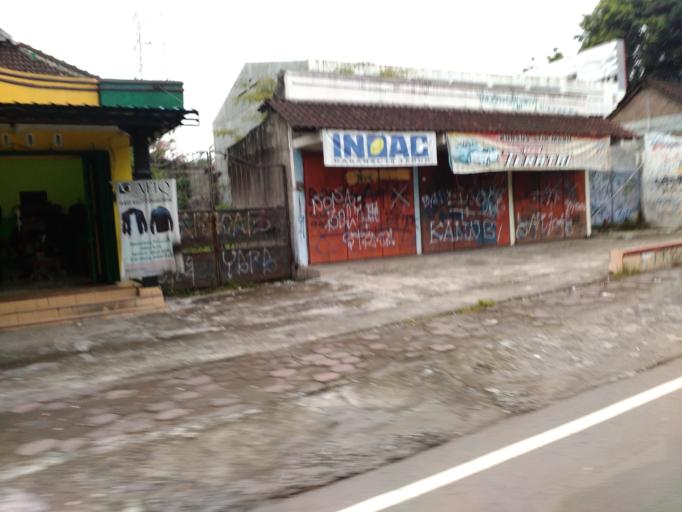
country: ID
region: Central Java
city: Boyolali
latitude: -7.5180
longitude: 110.5933
